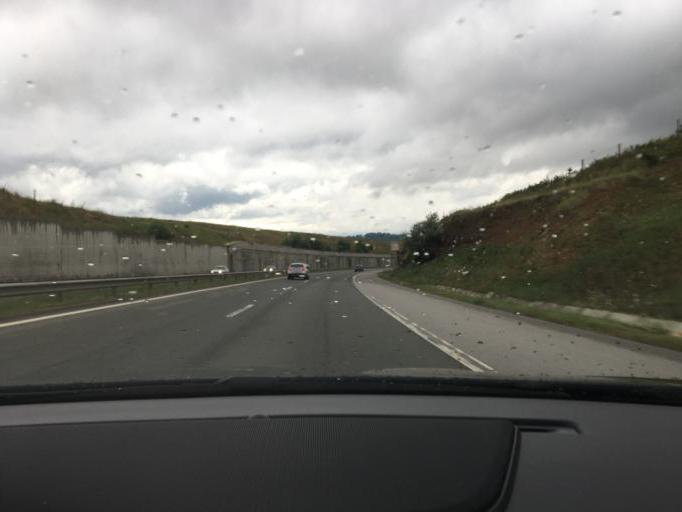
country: BG
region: Pernik
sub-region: Obshtina Pernik
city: Pernik
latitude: 42.6180
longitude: 23.1397
